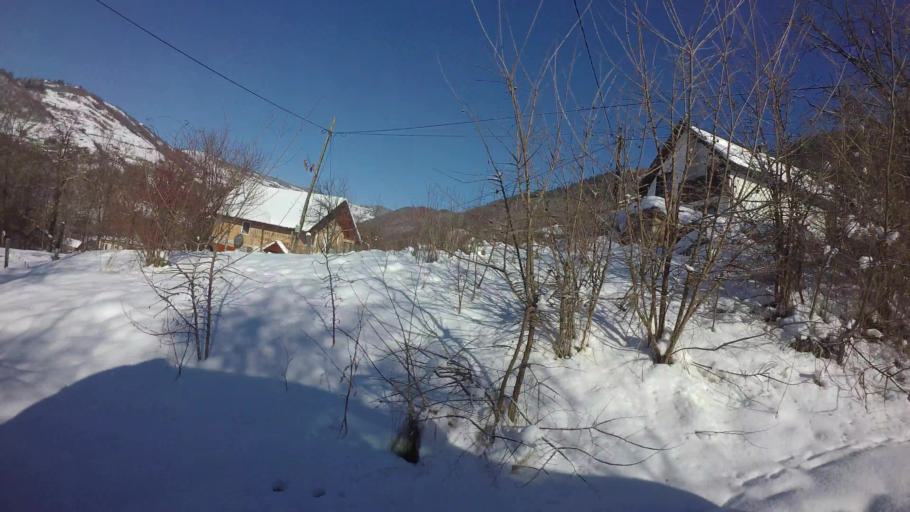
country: BA
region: Federation of Bosnia and Herzegovina
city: Kobilja Glava
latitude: 43.8963
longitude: 18.4167
